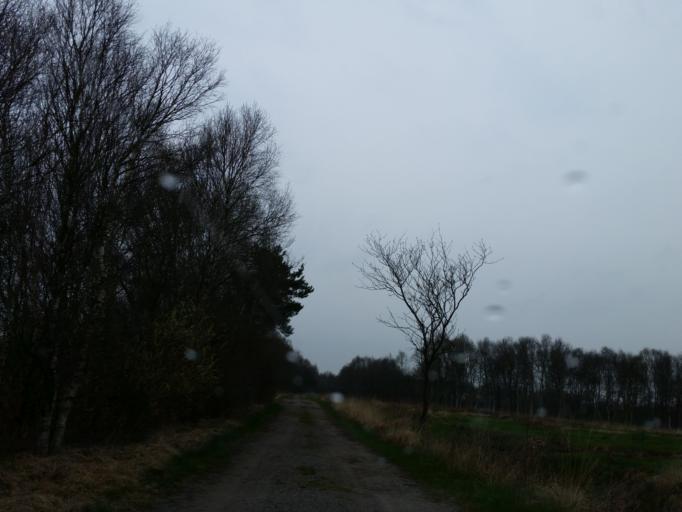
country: DE
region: Lower Saxony
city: Mittelstenahe
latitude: 53.6001
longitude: 9.0017
